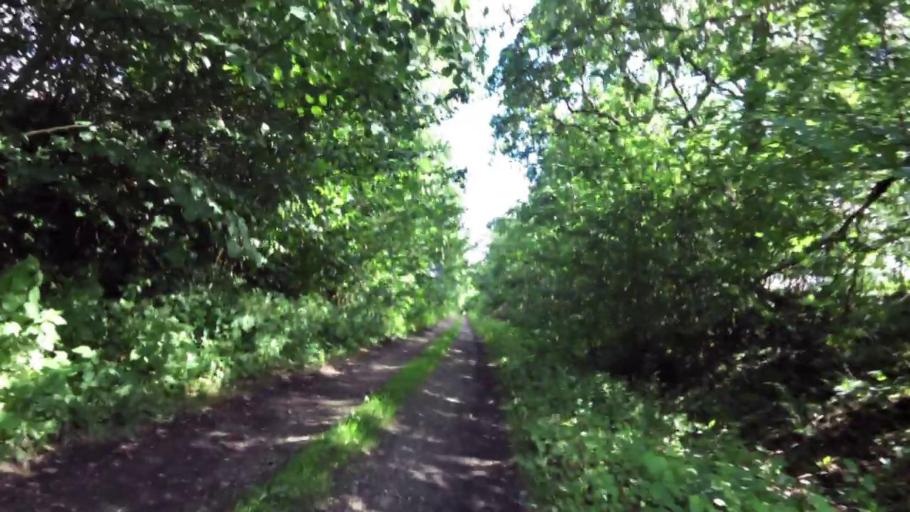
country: PL
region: West Pomeranian Voivodeship
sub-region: Powiat slawienski
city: Slawno
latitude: 54.5058
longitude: 16.7044
